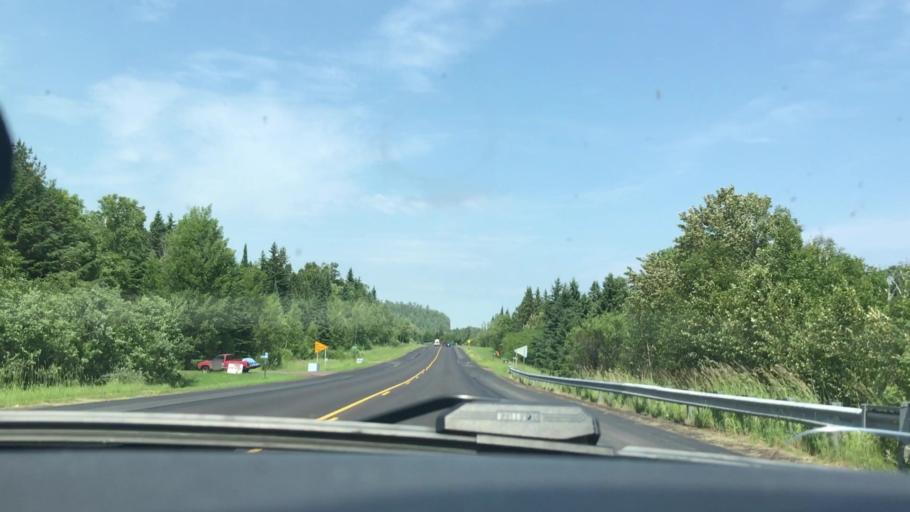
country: US
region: Minnesota
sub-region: Lake County
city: Silver Bay
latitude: 47.3578
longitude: -91.1785
